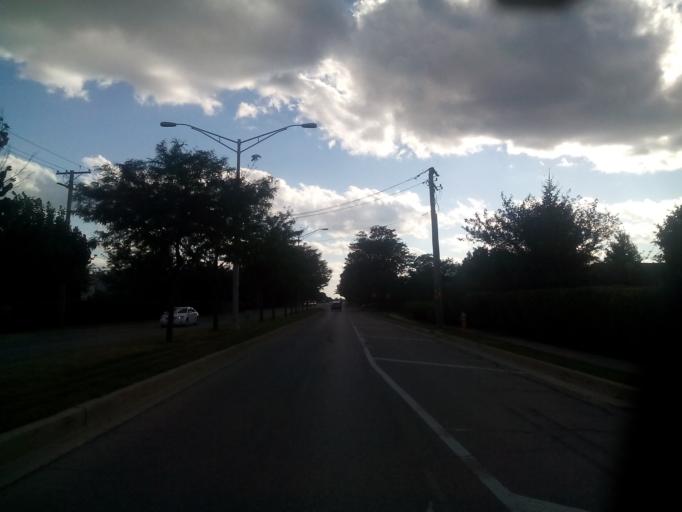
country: US
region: Illinois
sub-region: Will County
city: Romeoville
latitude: 41.6961
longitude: -88.1477
